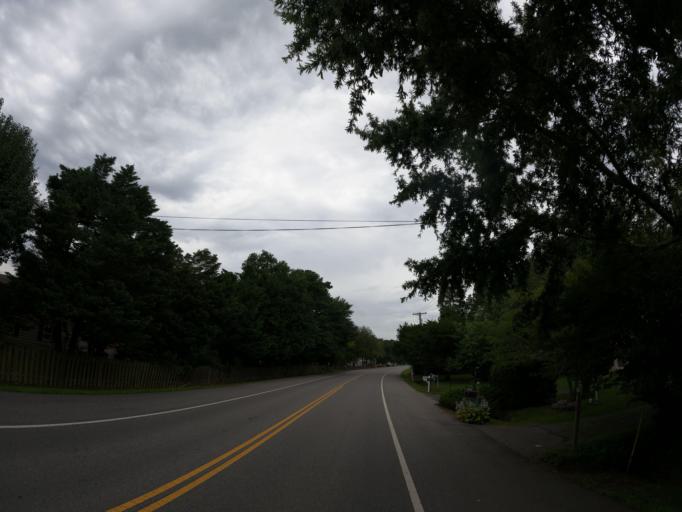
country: US
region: Maryland
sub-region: Saint Mary's County
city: Lexington Park
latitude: 38.1411
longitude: -76.5062
